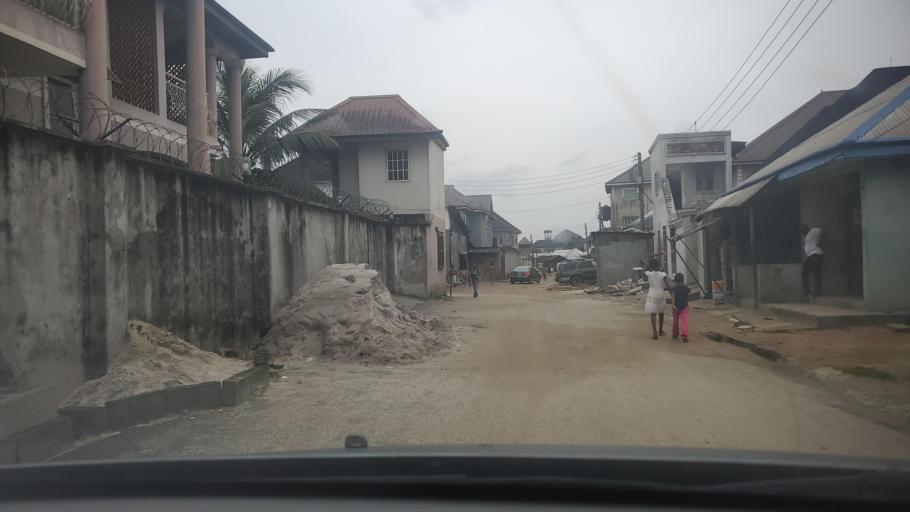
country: NG
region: Rivers
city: Port Harcourt
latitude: 4.8436
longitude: 7.0003
